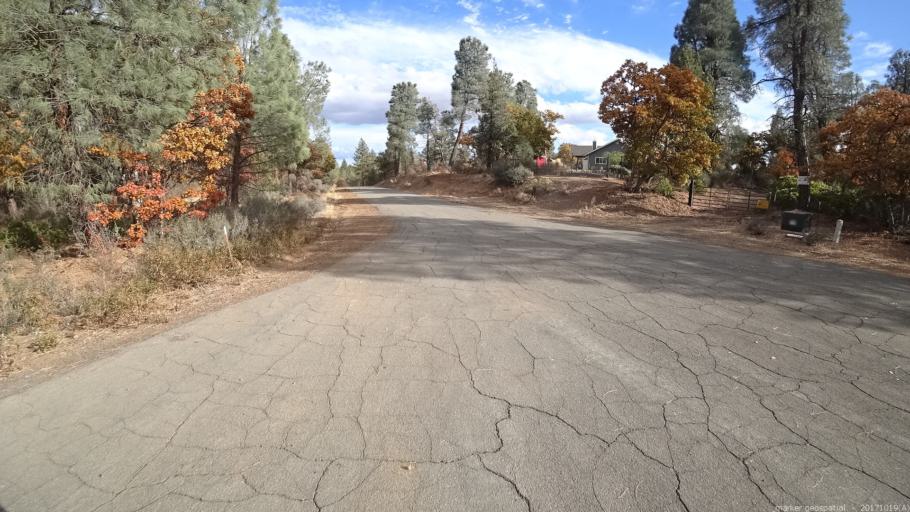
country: US
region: California
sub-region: Shasta County
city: Burney
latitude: 40.9591
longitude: -121.4424
